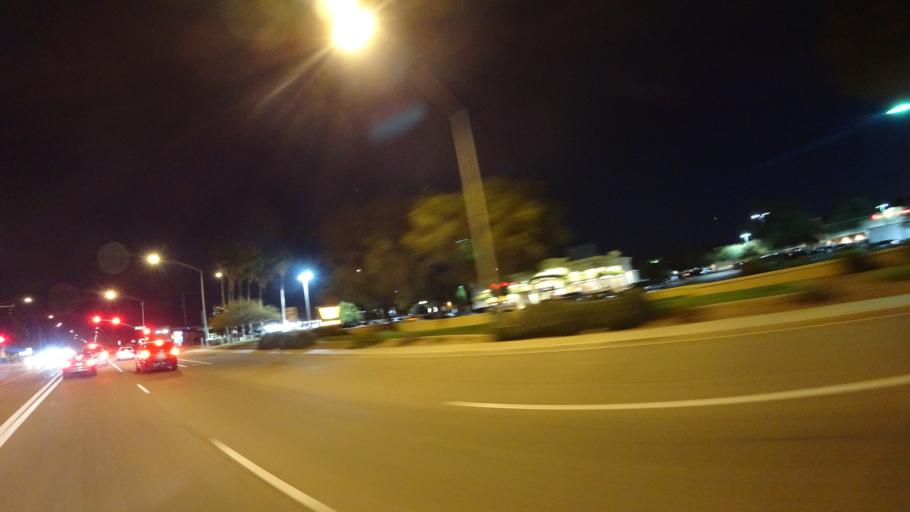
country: US
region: Arizona
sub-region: Maricopa County
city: Mesa
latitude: 33.4518
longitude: -111.7023
